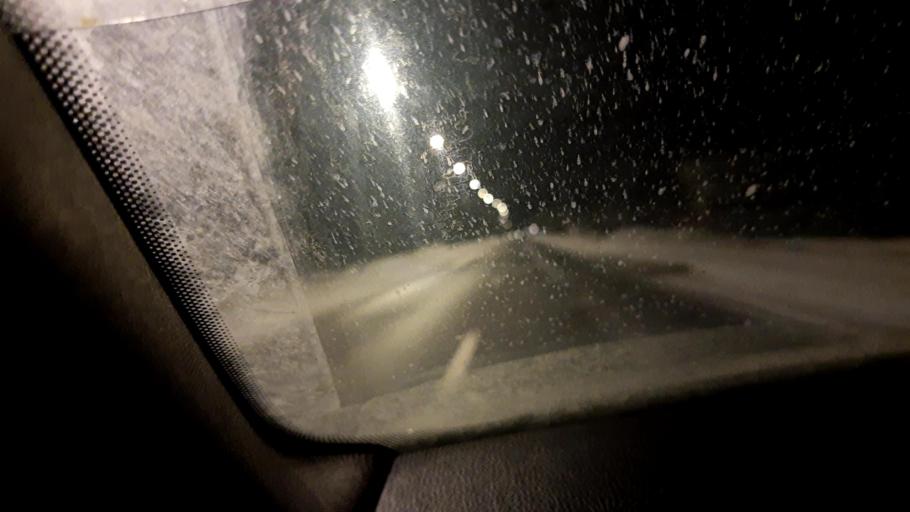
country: RU
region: Moskovskaya
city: Bogorodskoye
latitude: 56.6450
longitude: 38.1640
